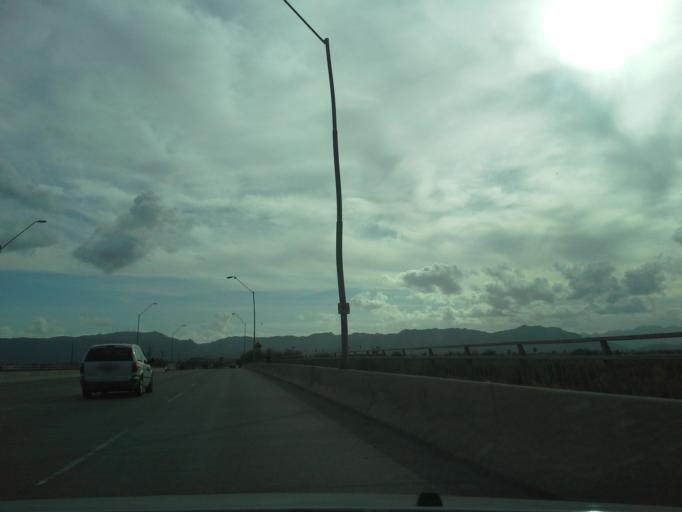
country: US
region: Arizona
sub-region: Maricopa County
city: Phoenix
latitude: 33.4197
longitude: -112.0824
